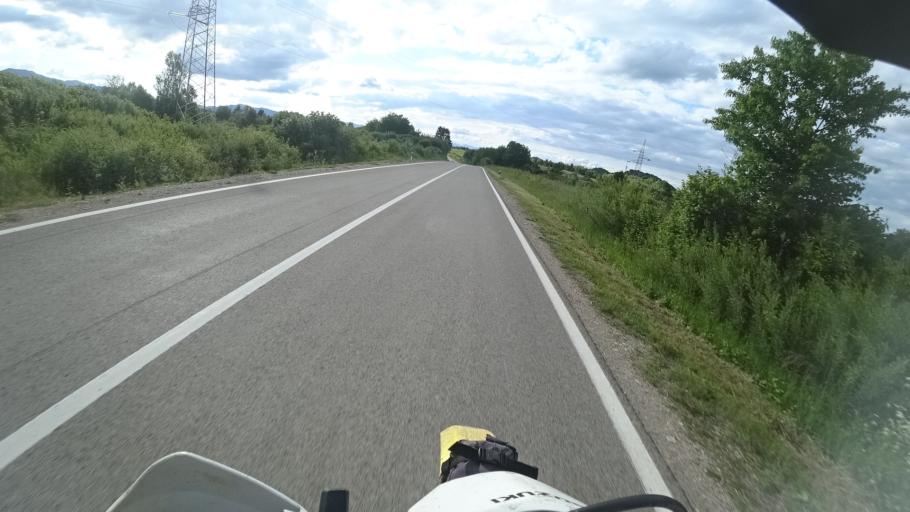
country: HR
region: Licko-Senjska
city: Gospic
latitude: 44.5005
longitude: 15.4529
